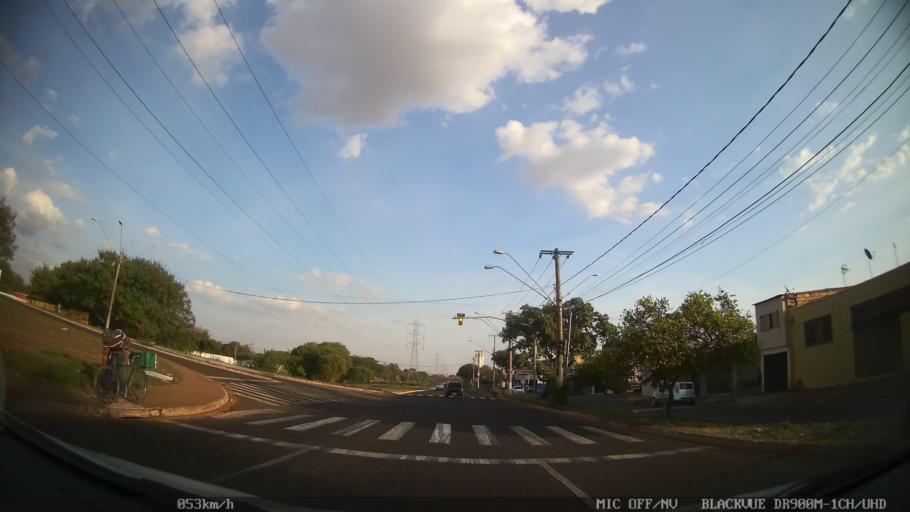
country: BR
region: Sao Paulo
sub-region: Ribeirao Preto
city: Ribeirao Preto
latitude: -21.1271
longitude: -47.8036
